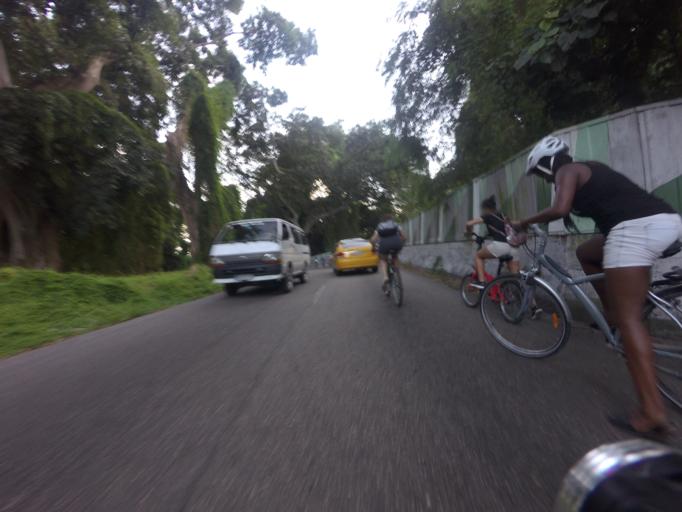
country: CU
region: La Habana
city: Cerro
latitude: 23.1116
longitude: -82.4067
